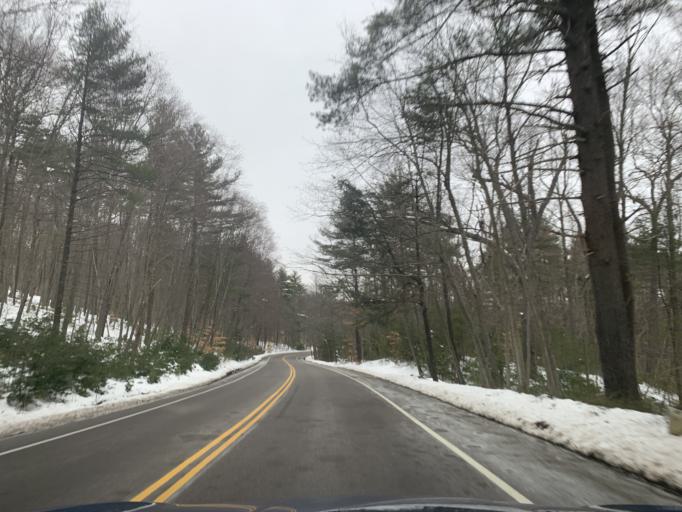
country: US
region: Massachusetts
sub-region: Norfolk County
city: Milton
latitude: 42.2249
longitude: -71.0933
